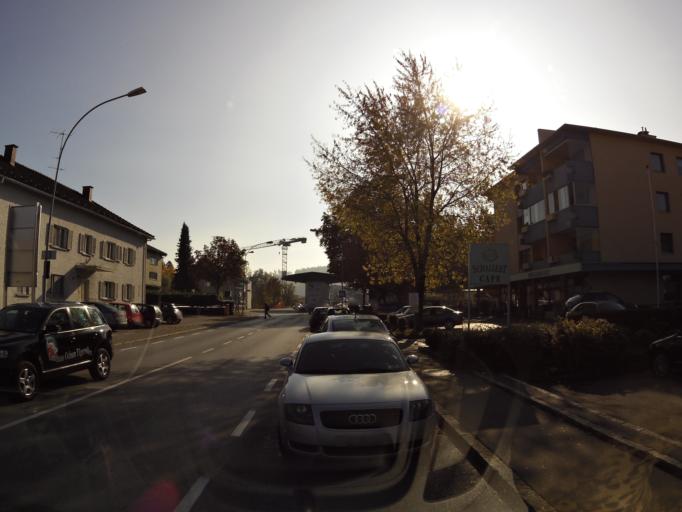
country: AT
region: Vorarlberg
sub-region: Politischer Bezirk Bregenz
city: Hochst
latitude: 47.4581
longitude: 9.6396
